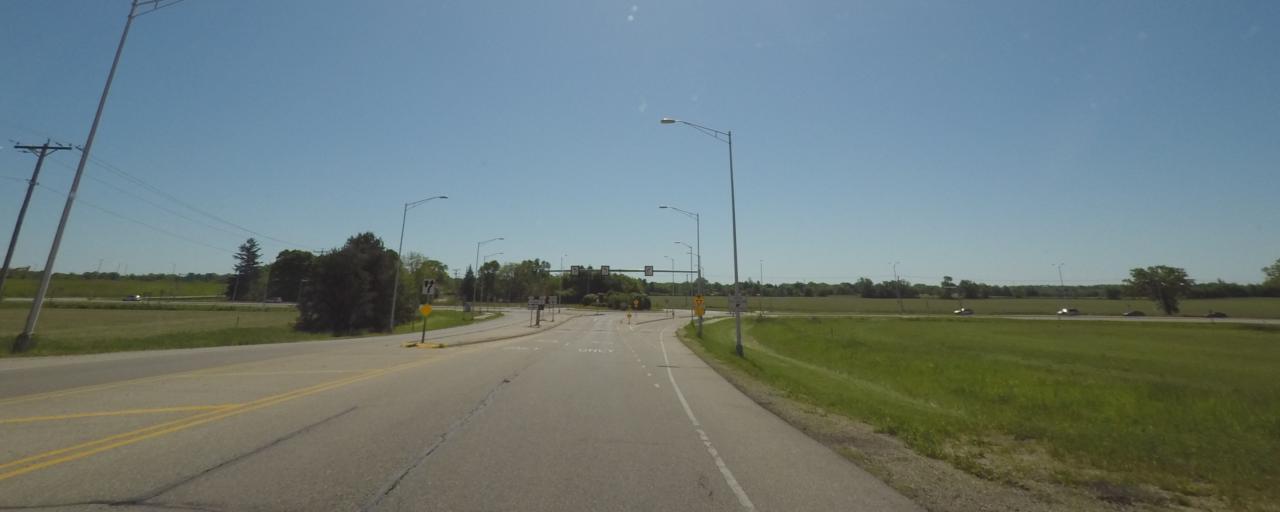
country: US
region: Wisconsin
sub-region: Dane County
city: Oregon
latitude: 42.9502
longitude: -89.3818
